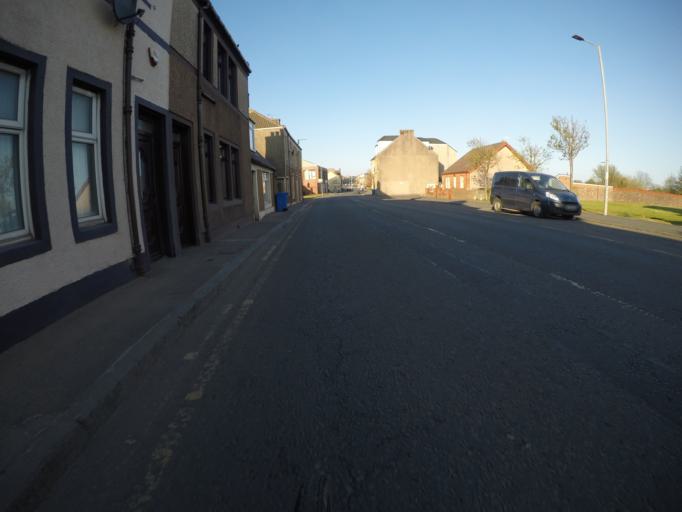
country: GB
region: Scotland
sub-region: North Ayrshire
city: Stevenston
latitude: 55.6397
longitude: -4.7603
